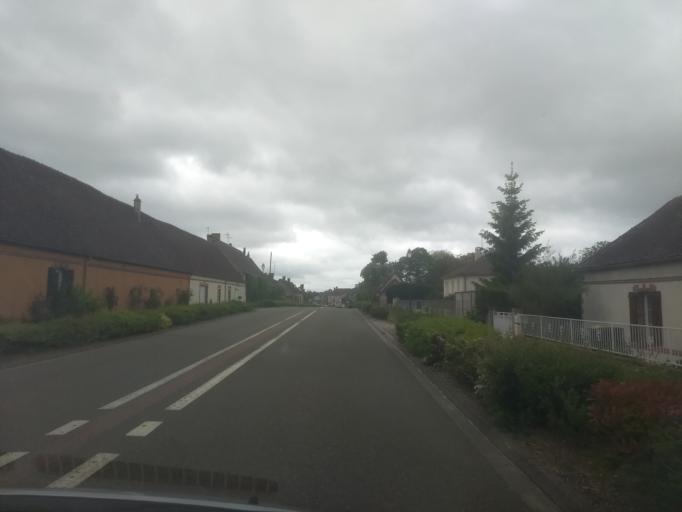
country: FR
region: Centre
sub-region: Departement d'Eure-et-Loir
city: Chateauneuf-en-Thymerais
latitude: 48.5384
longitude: 1.1583
